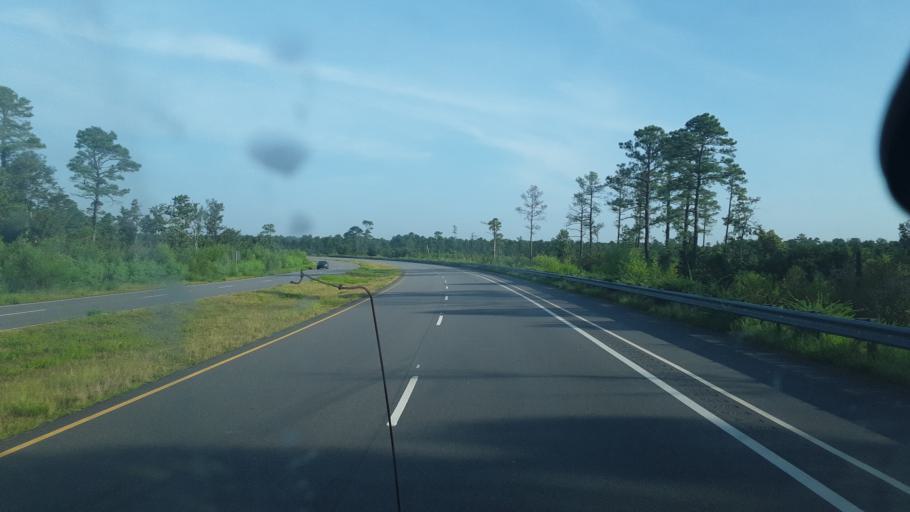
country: US
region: South Carolina
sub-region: Horry County
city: Forestbrook
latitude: 33.7974
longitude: -78.8827
